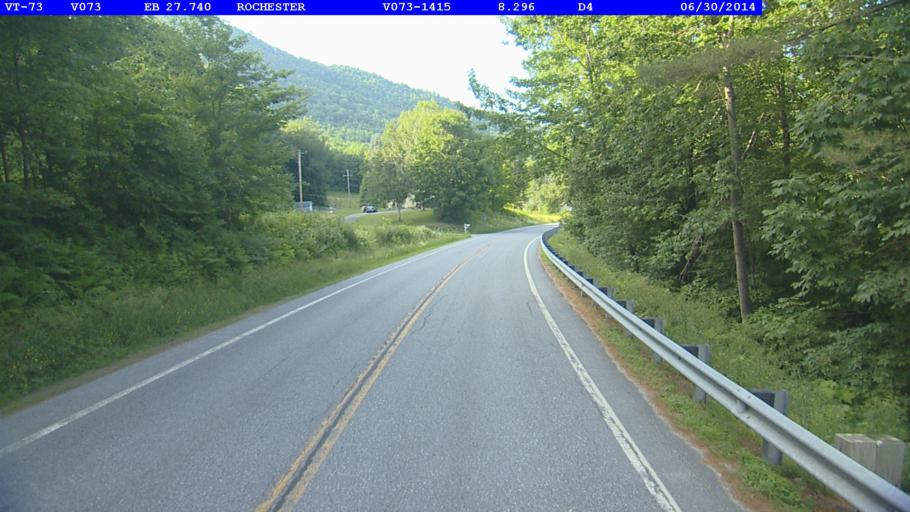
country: US
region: Vermont
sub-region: Orange County
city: Randolph
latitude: 43.8595
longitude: -72.8162
